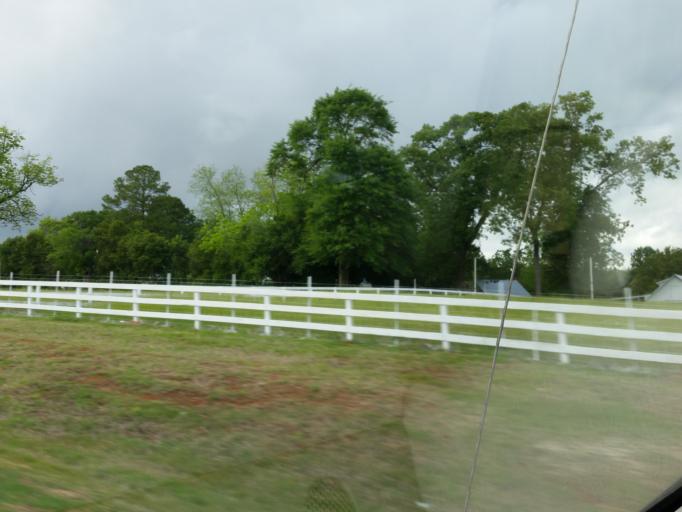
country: US
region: Georgia
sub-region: Dooly County
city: Unadilla
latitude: 32.3417
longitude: -83.7862
